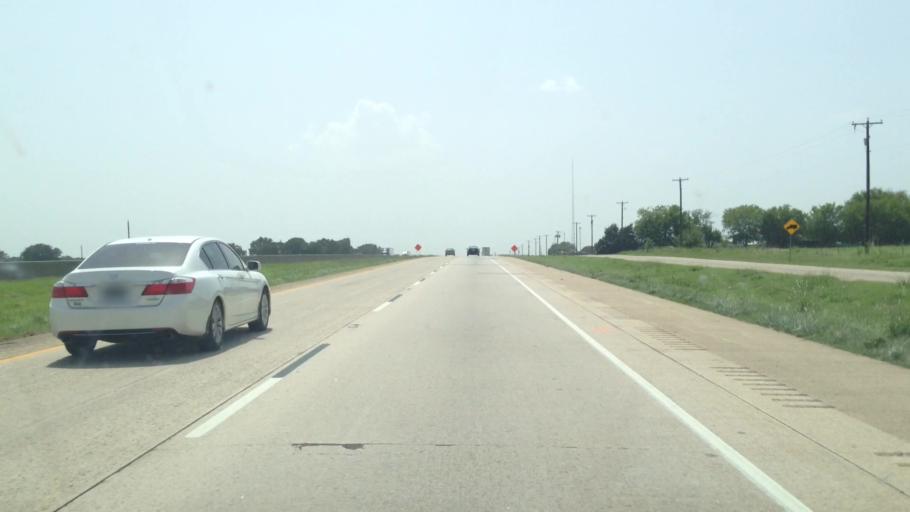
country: US
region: Texas
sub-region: Hopkins County
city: Sulphur Springs
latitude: 33.1209
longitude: -95.6978
